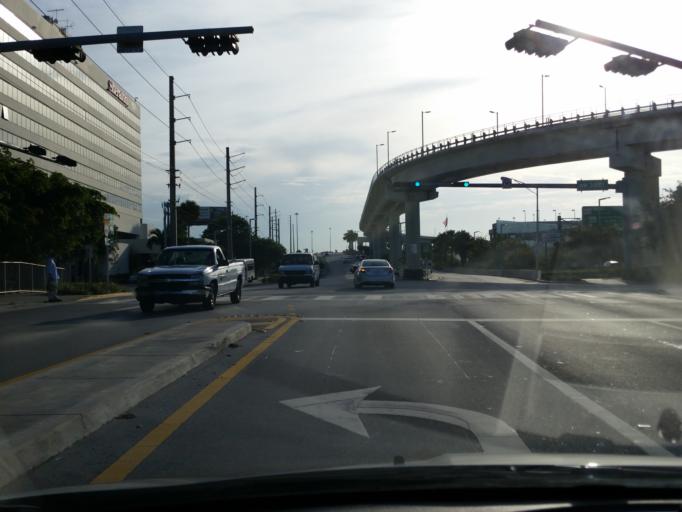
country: US
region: Florida
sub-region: Miami-Dade County
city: Brownsville
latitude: 25.7950
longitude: -80.2585
